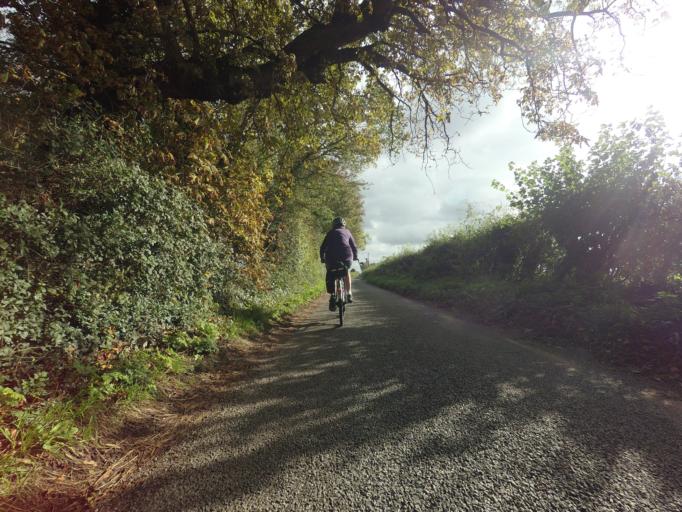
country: GB
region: England
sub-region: Norfolk
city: Snettisham
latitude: 52.8632
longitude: 0.5106
